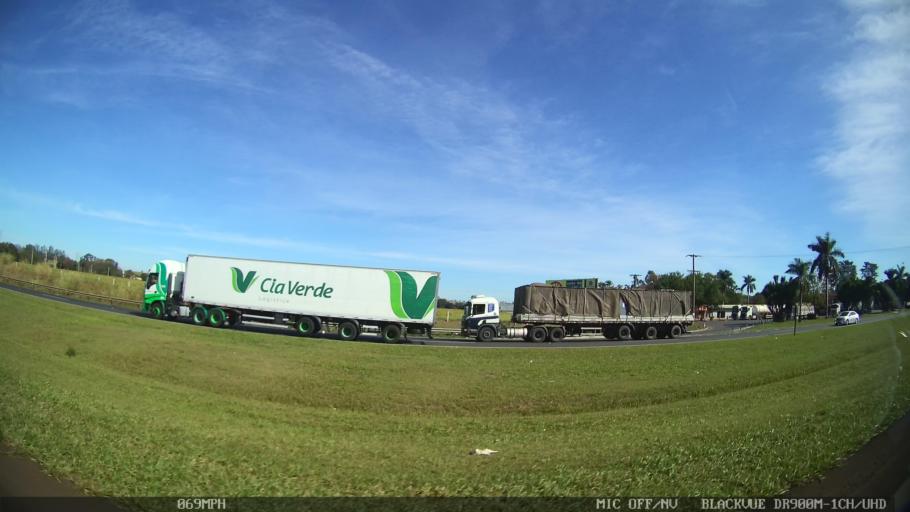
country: BR
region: Sao Paulo
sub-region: Leme
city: Leme
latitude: -22.2261
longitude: -47.3916
